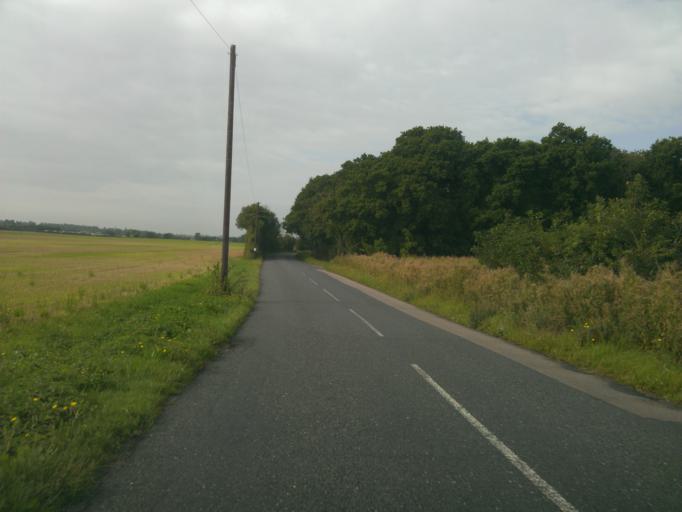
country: GB
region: England
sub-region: Essex
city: Great Bentley
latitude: 51.8291
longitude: 1.0742
